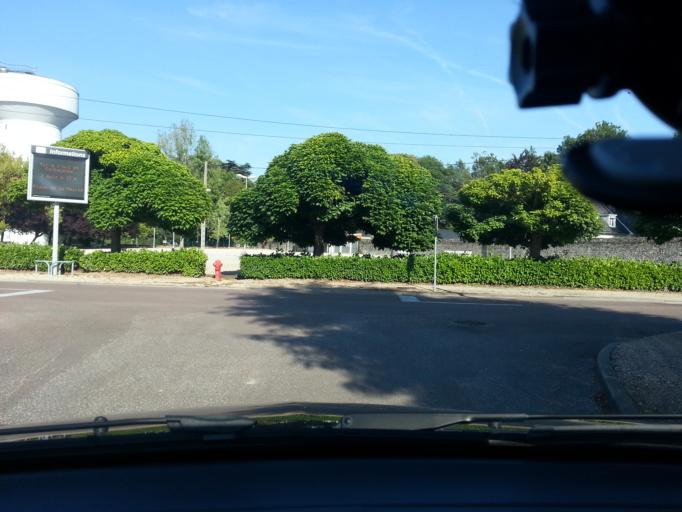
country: FR
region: Bourgogne
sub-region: Departement de Saone-et-Loire
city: Saint-Remy
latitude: 46.7711
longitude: 4.8143
